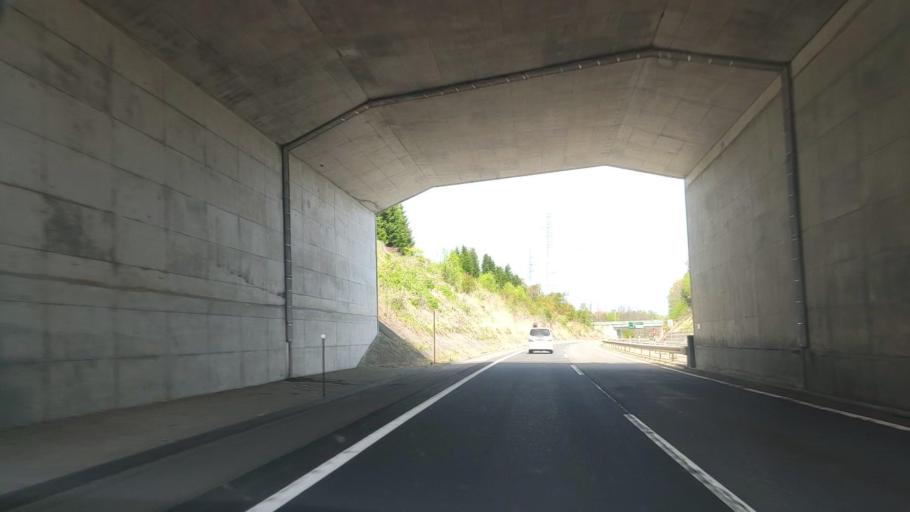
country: JP
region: Aomori
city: Hachinohe
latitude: 40.4790
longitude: 141.4593
